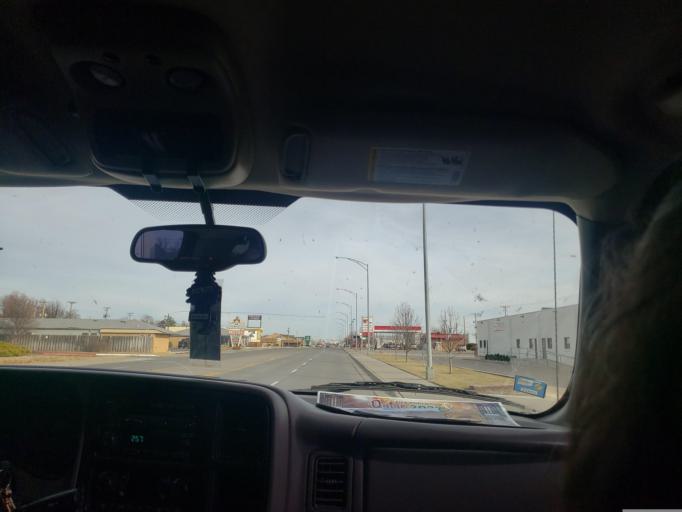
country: US
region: Kansas
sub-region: Ford County
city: Dodge City
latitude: 37.7543
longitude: -100.0460
